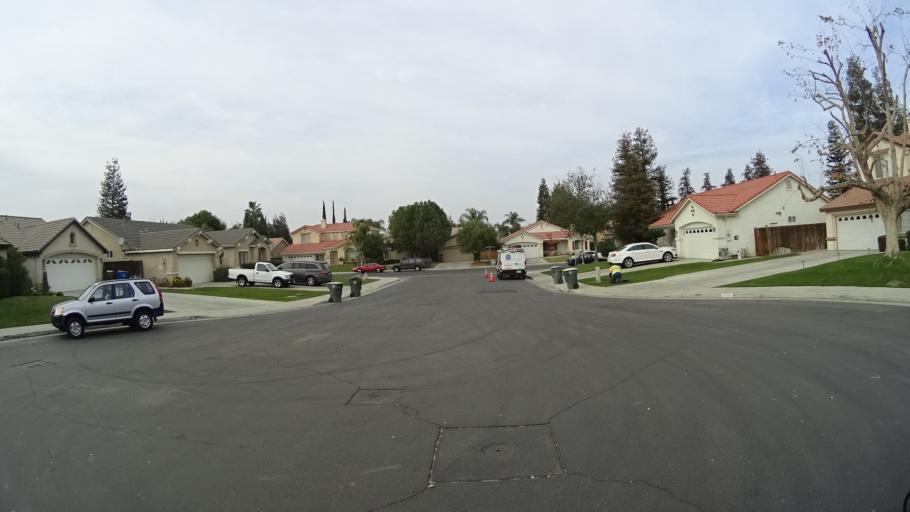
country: US
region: California
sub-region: Kern County
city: Rosedale
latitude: 35.3438
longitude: -119.1313
